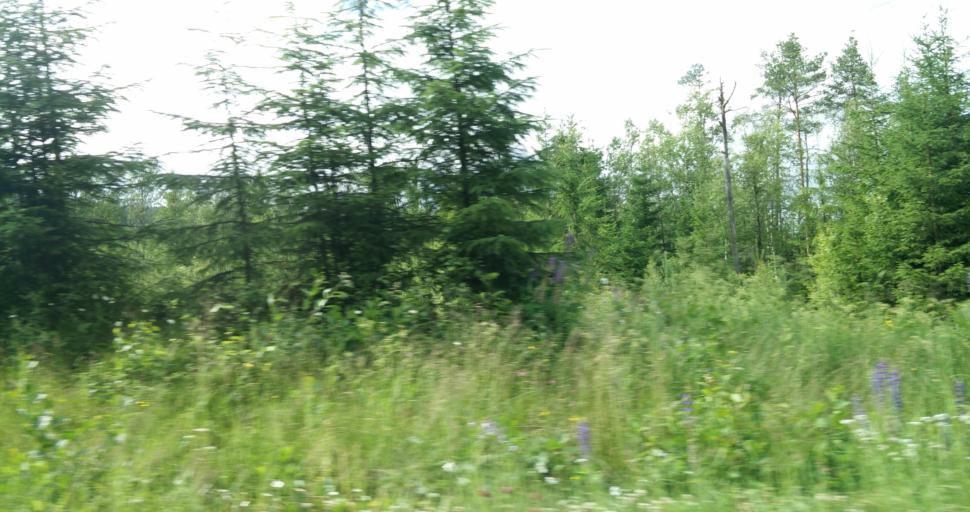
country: SE
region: Vaermland
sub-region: Hagfors Kommun
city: Ekshaerad
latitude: 60.0335
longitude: 13.4887
